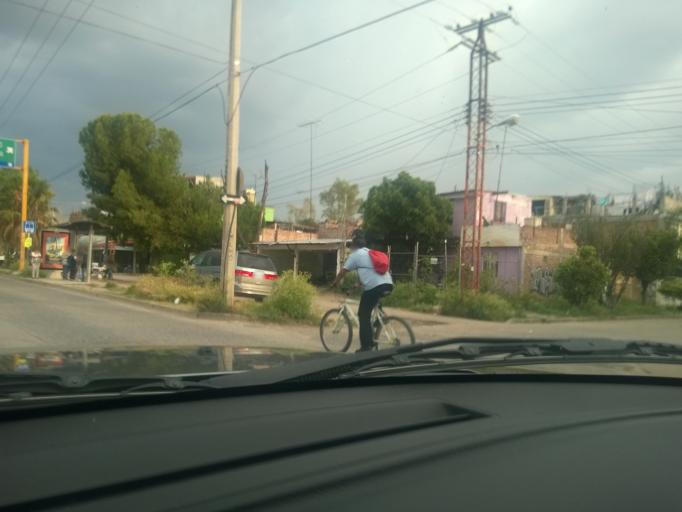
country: MX
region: Guanajuato
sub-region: Leon
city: Medina
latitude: 21.1153
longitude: -101.6289
